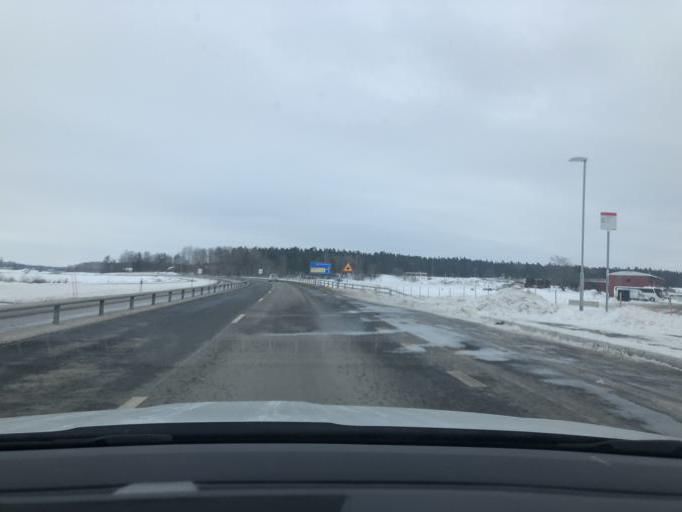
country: SE
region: OEstergoetland
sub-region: Linkopings Kommun
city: Sturefors
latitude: 58.3970
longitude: 15.7176
